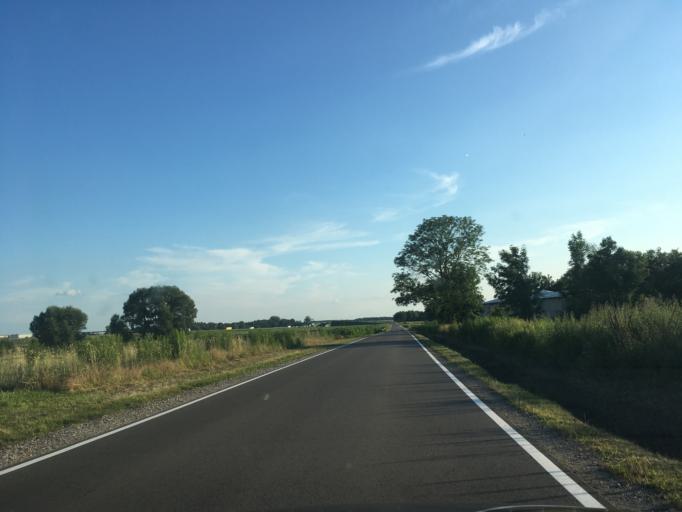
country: PL
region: Masovian Voivodeship
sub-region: Powiat warszawski zachodni
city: Blonie
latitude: 52.1493
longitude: 20.6034
